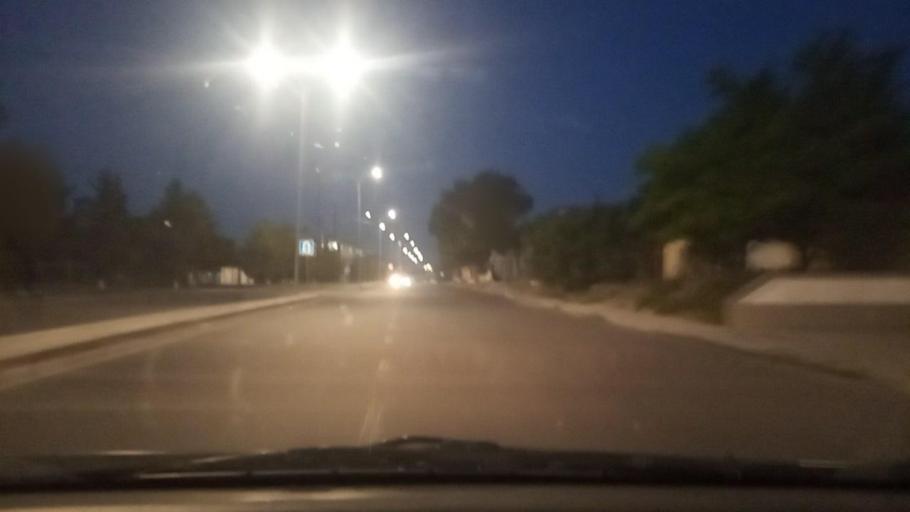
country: UZ
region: Toshkent Shahri
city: Tashkent
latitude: 41.2513
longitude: 69.2135
